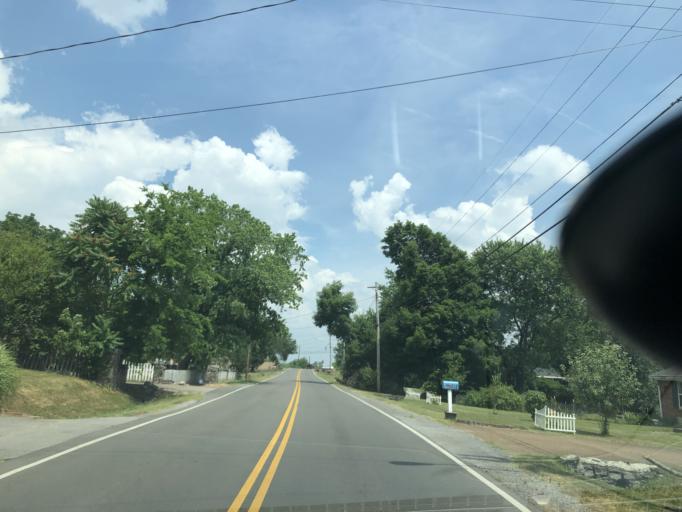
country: US
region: Tennessee
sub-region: Davidson County
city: Oak Hill
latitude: 36.0711
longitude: -86.6961
